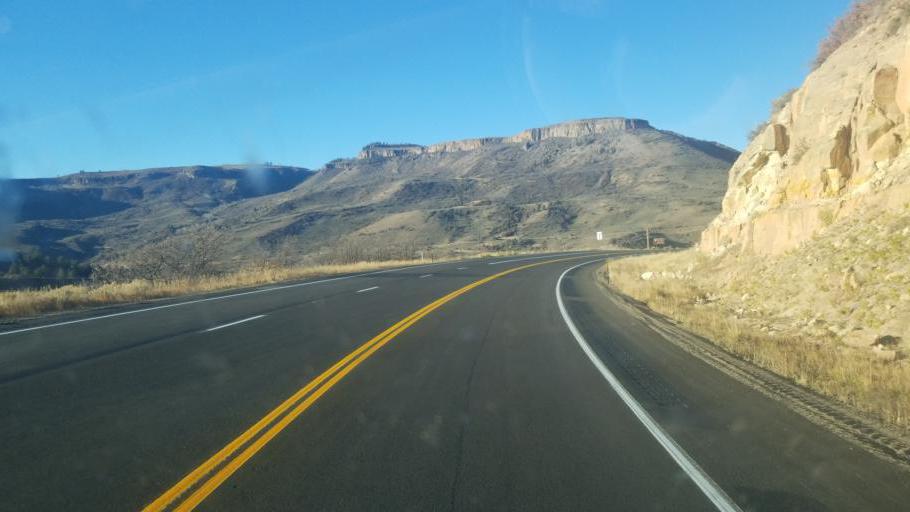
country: US
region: Colorado
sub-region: Hinsdale County
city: Lake City
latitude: 38.4438
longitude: -107.3420
